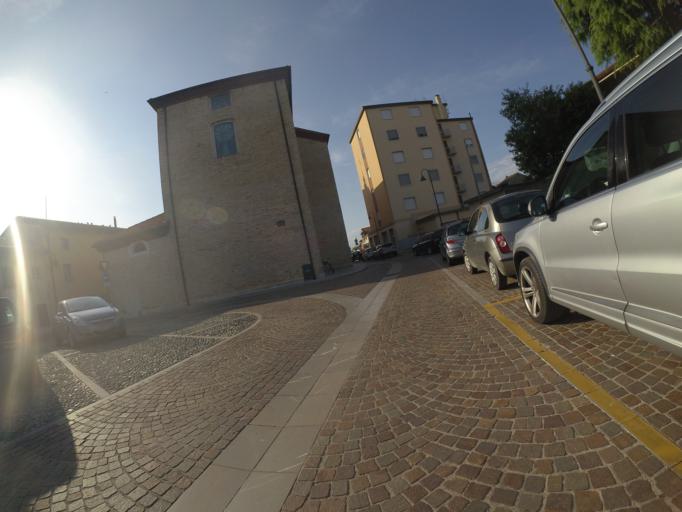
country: IT
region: Friuli Venezia Giulia
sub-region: Provincia di Udine
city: Mortegliano
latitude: 45.9443
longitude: 13.1729
